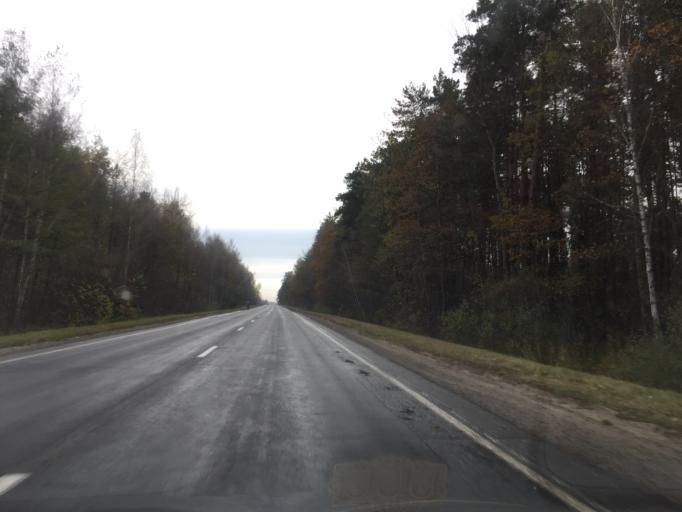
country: BY
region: Gomel
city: Kastsyukowka
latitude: 52.4260
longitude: 30.8281
